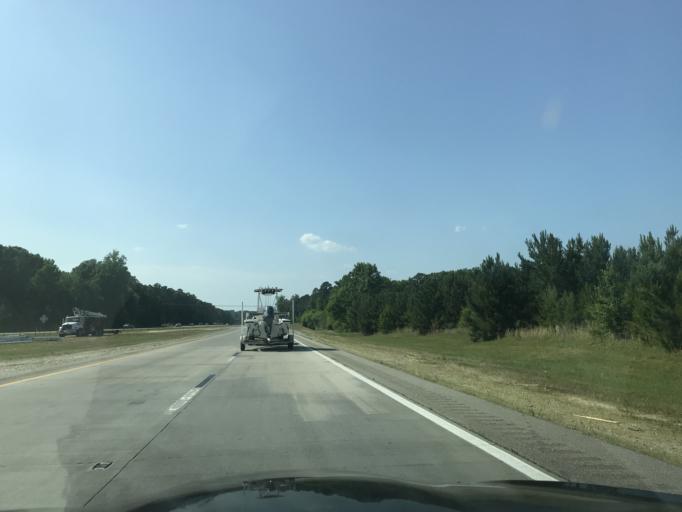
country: US
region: North Carolina
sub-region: Wake County
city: Knightdale
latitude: 35.7732
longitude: -78.5064
